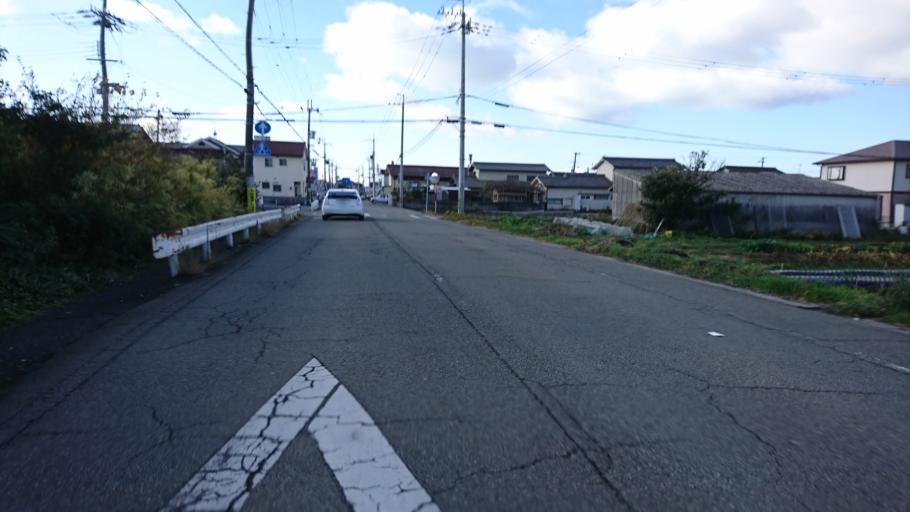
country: JP
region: Hyogo
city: Kakogawacho-honmachi
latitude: 34.7501
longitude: 134.8167
